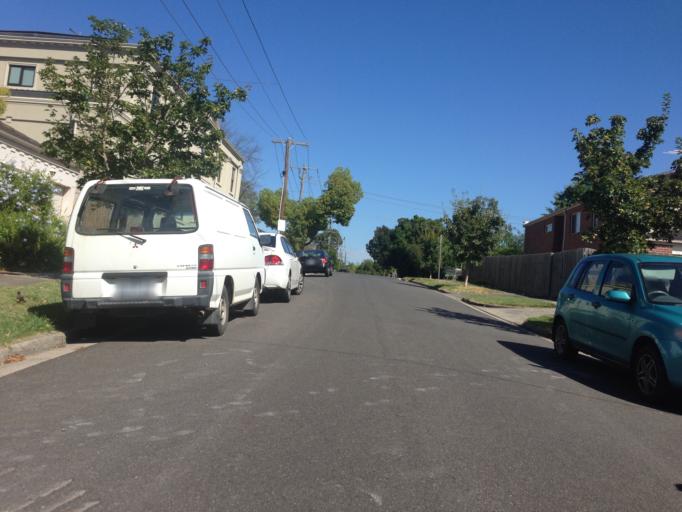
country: AU
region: Victoria
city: Balwyn
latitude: -37.8048
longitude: 145.0754
